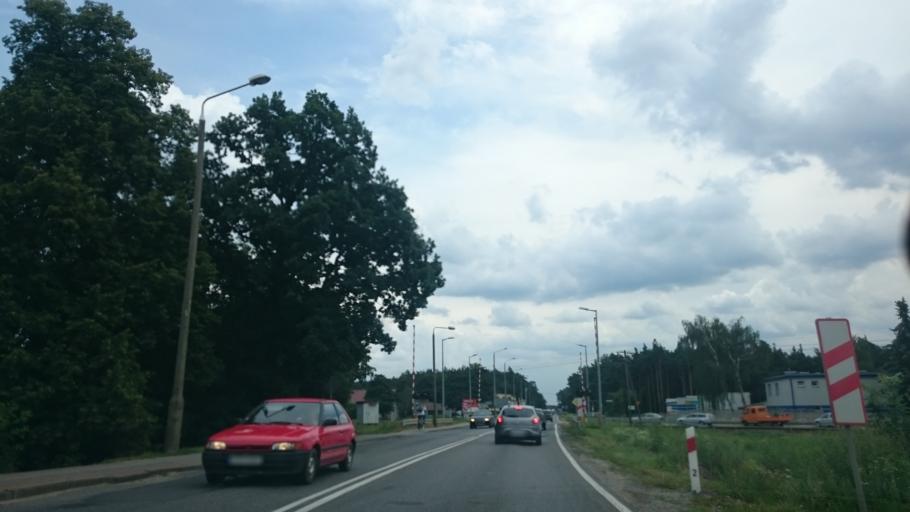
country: PL
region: Kujawsko-Pomorskie
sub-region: Powiat tucholski
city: Tuchola
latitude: 53.5786
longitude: 17.8771
